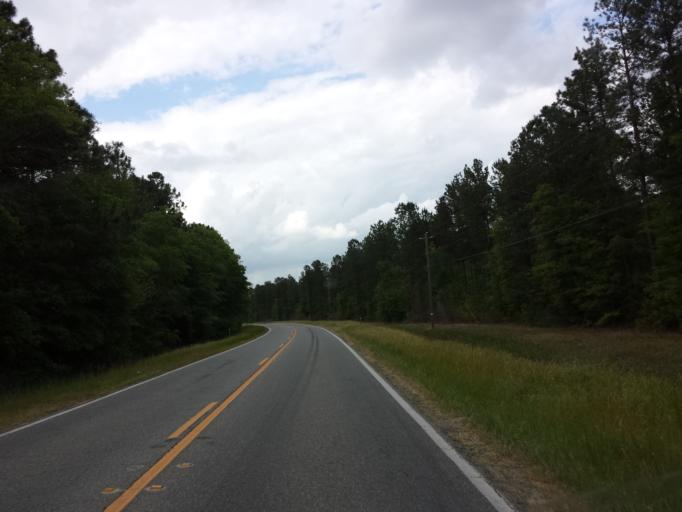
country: US
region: Georgia
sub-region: Cook County
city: Sparks
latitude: 31.2065
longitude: -83.4506
